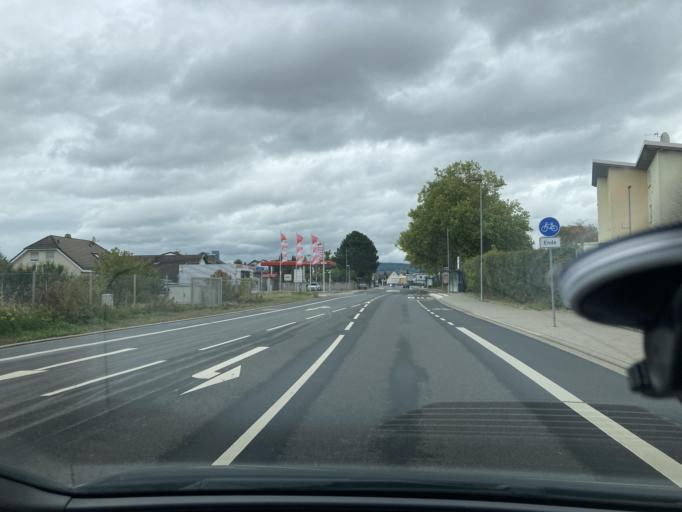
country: DE
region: Hesse
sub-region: Regierungsbezirk Darmstadt
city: Seligenstadt
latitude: 50.0400
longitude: 8.9932
